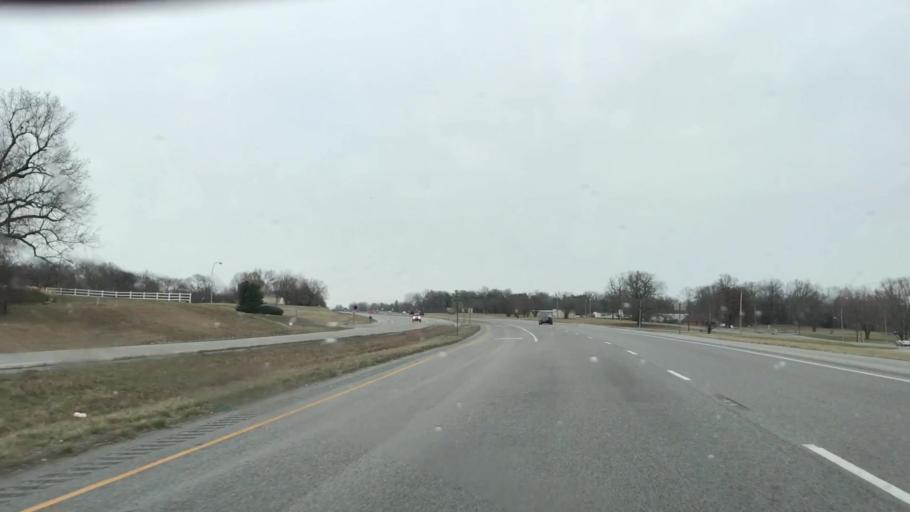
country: US
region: Kentucky
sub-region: Trigg County
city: Cadiz
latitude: 36.8667
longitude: -87.7801
